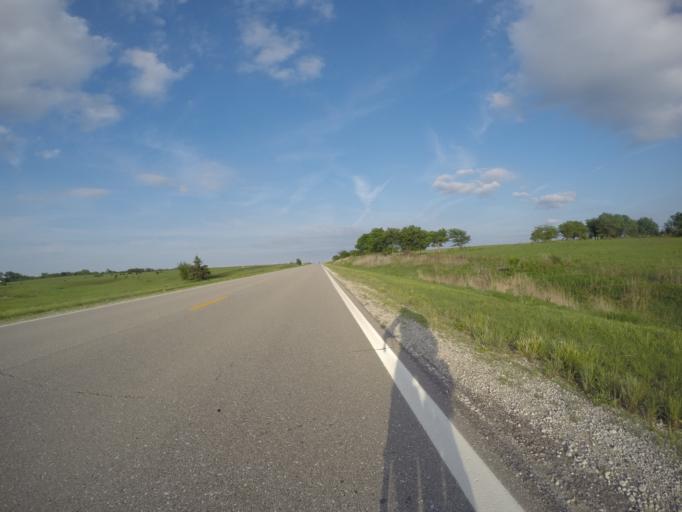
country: US
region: Kansas
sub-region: Pottawatomie County
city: Westmoreland
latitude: 39.4283
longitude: -96.5638
